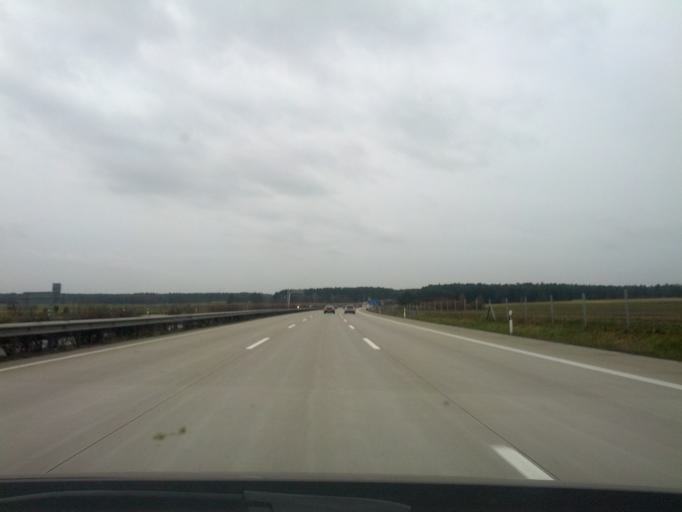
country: DE
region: Lower Saxony
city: Egestorf
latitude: 53.1600
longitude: 10.0616
